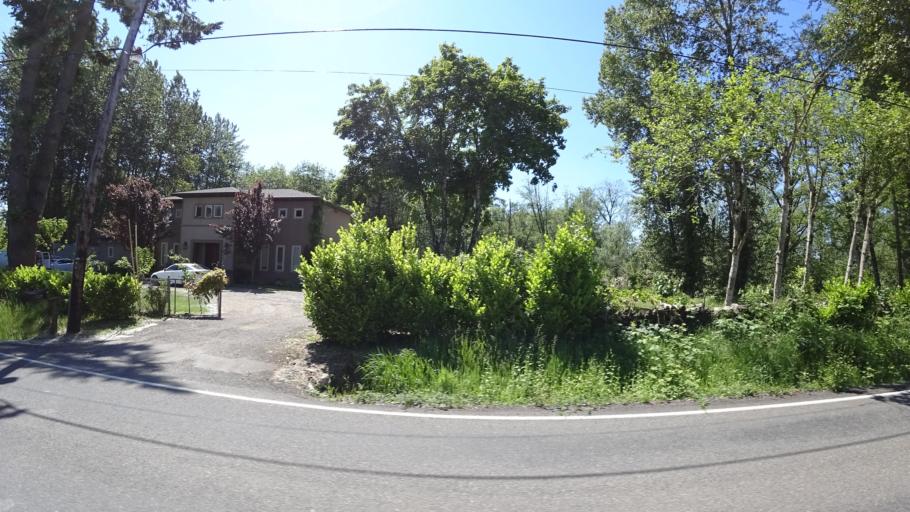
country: US
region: Oregon
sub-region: Clackamas County
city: Damascus
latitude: 45.4679
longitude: -122.4754
